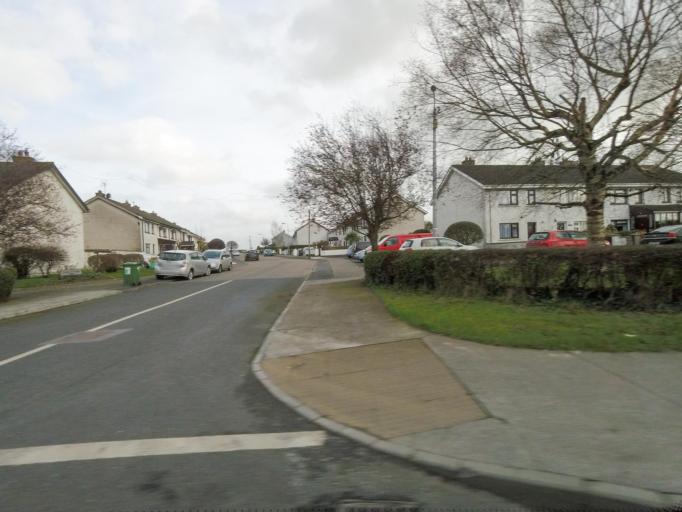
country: IE
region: Leinster
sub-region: Kildare
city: Kilcullen
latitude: 53.1282
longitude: -6.7479
